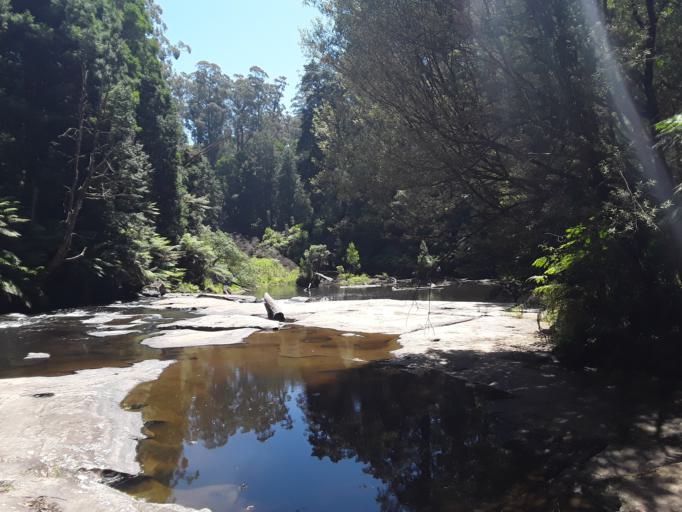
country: AU
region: Victoria
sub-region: Colac-Otway
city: Apollo Bay
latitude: -38.7028
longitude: 143.4778
